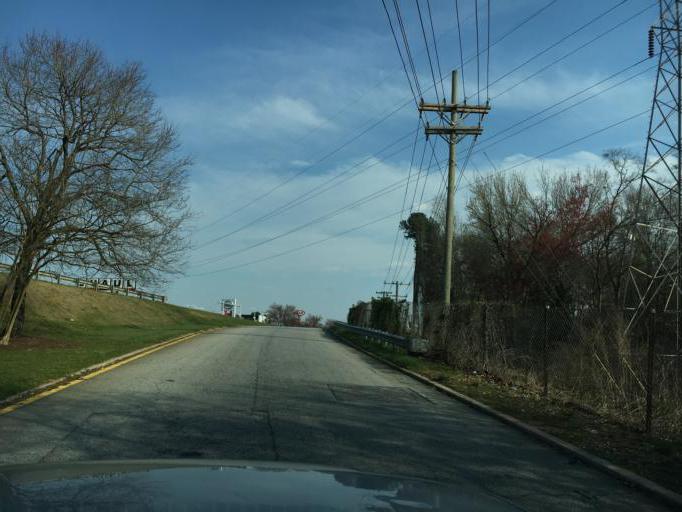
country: US
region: South Carolina
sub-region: Spartanburg County
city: Spartanburg
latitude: 34.9721
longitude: -81.9386
